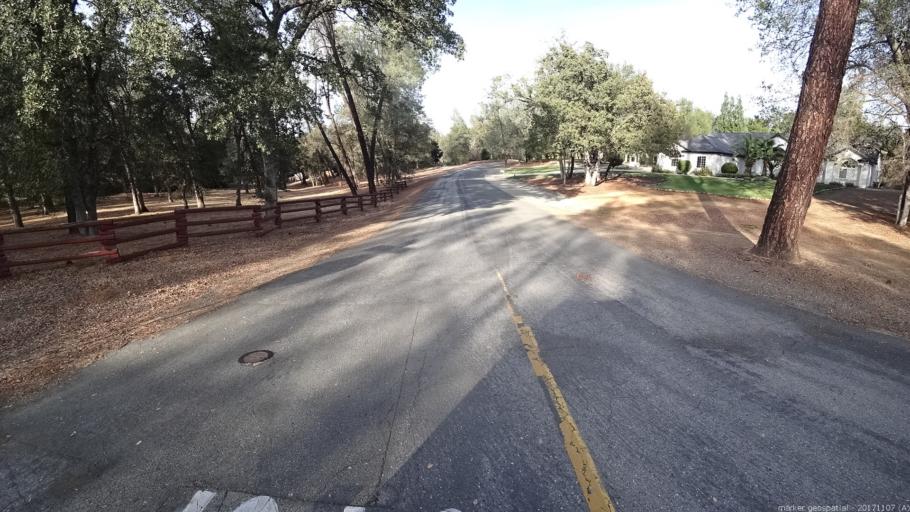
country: US
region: California
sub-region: Shasta County
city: Shasta
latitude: 40.5179
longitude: -122.4699
